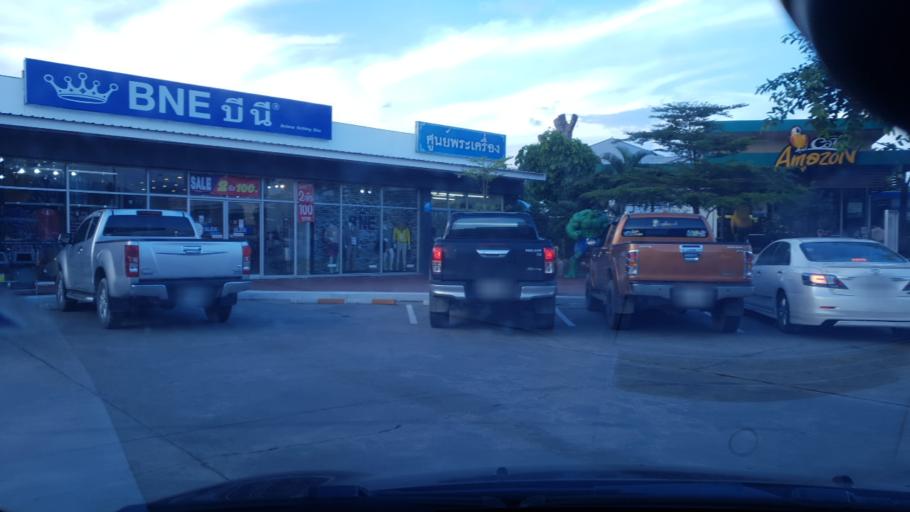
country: TH
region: Chiang Rai
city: Mae Suai
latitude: 19.6478
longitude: 99.5318
